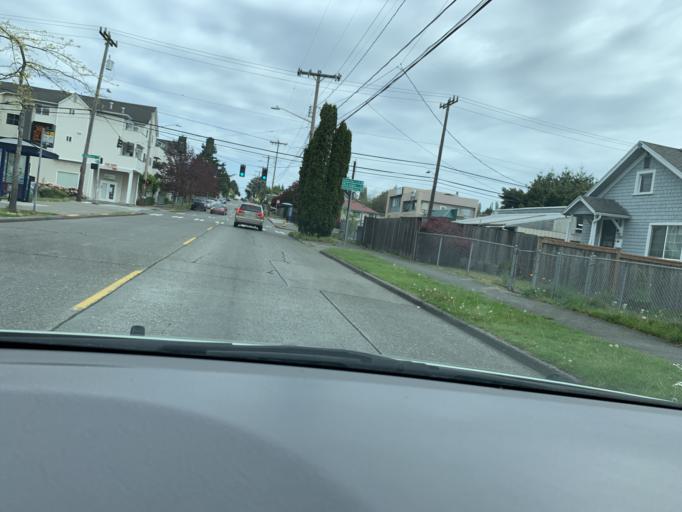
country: US
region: Washington
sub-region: King County
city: White Center
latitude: 47.5530
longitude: -122.3135
